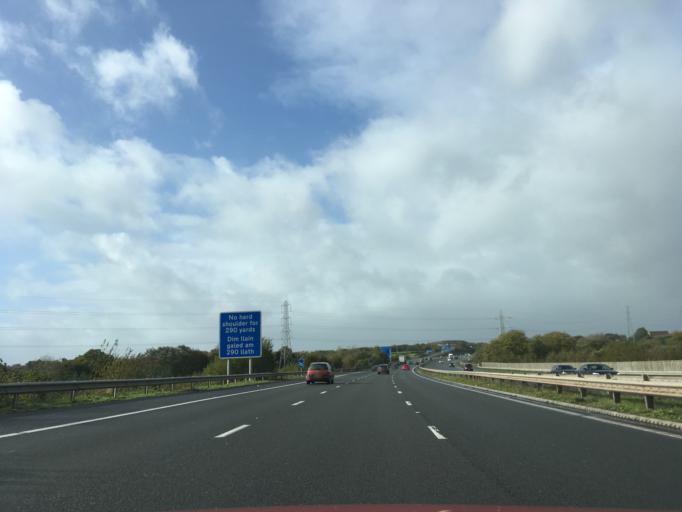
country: GB
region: Wales
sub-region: Newport
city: Marshfield
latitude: 51.5418
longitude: -3.1154
